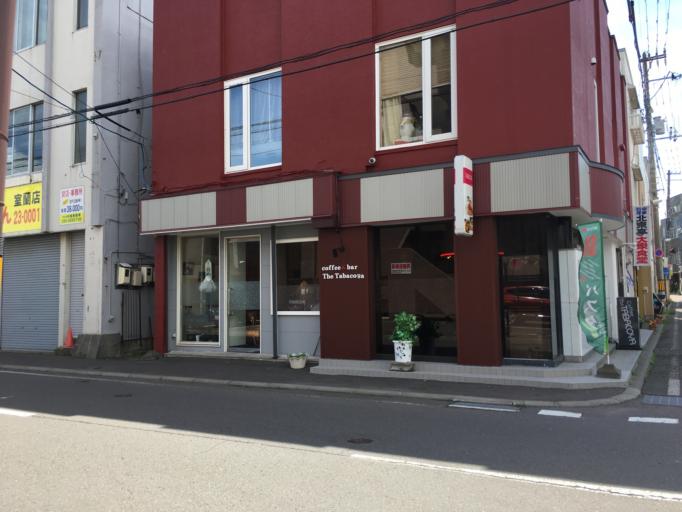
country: JP
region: Hokkaido
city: Muroran
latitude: 42.3170
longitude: 140.9730
